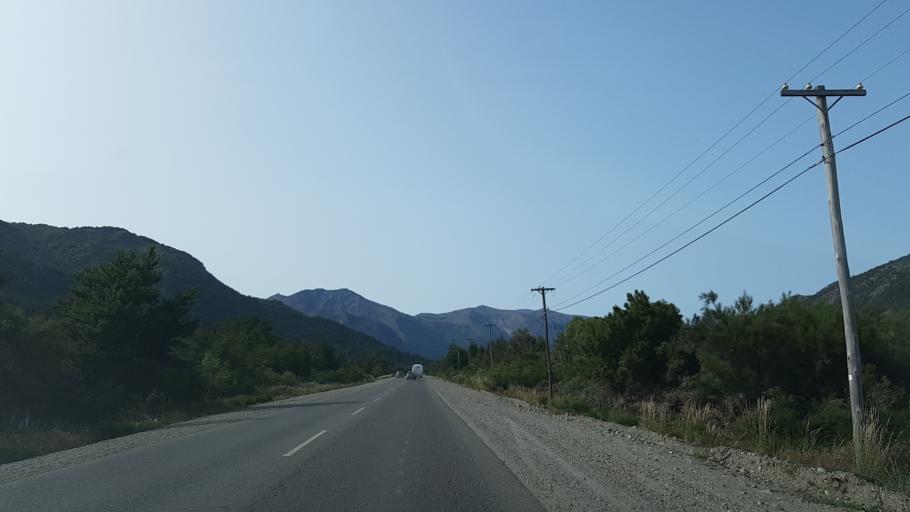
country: AR
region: Rio Negro
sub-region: Departamento de Bariloche
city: San Carlos de Bariloche
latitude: -41.1347
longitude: -71.4133
